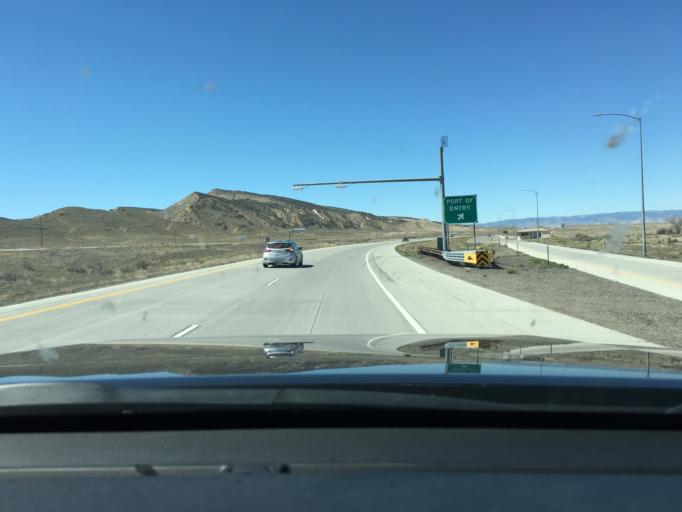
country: US
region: Colorado
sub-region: Mesa County
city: Loma
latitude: 39.1794
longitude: -108.8228
